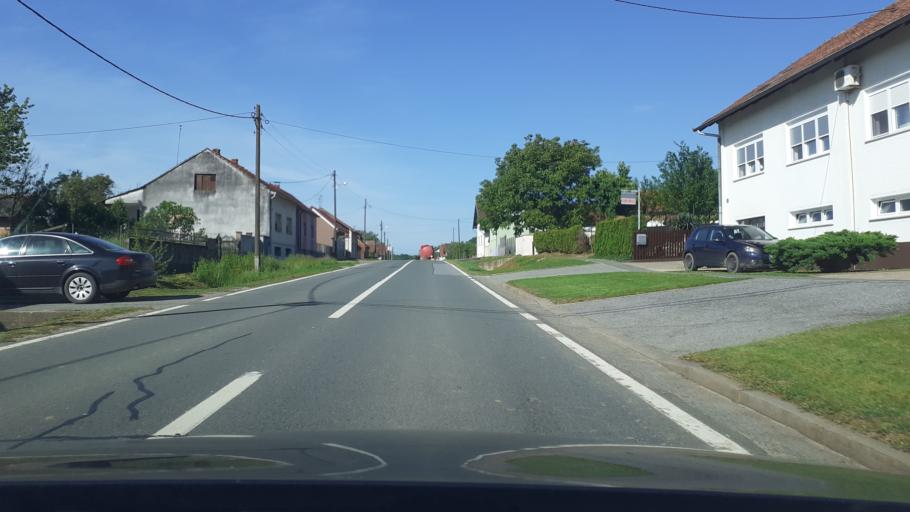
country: HR
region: Brodsko-Posavska
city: Batrina
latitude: 45.2152
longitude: 17.6975
